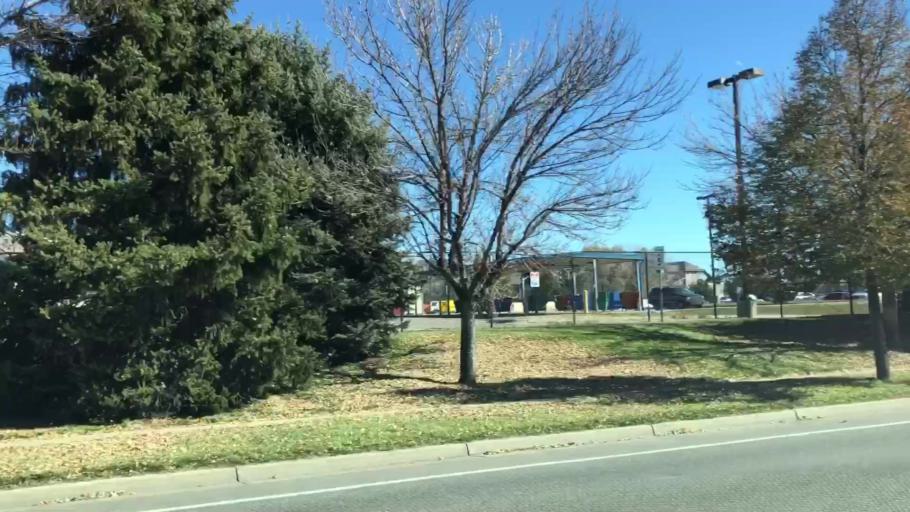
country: US
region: Colorado
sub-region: Larimer County
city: Fort Collins
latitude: 40.5305
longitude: -105.0742
